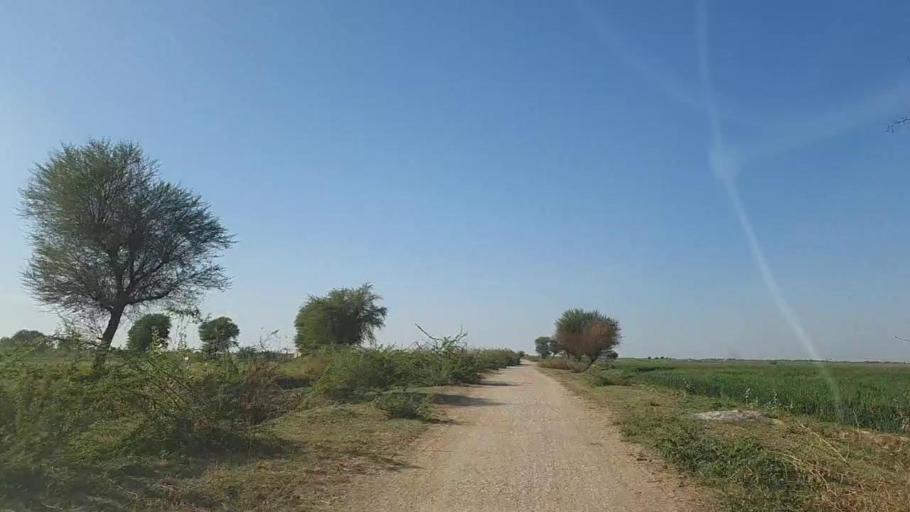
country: PK
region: Sindh
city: Kunri
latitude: 25.2294
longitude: 69.5070
